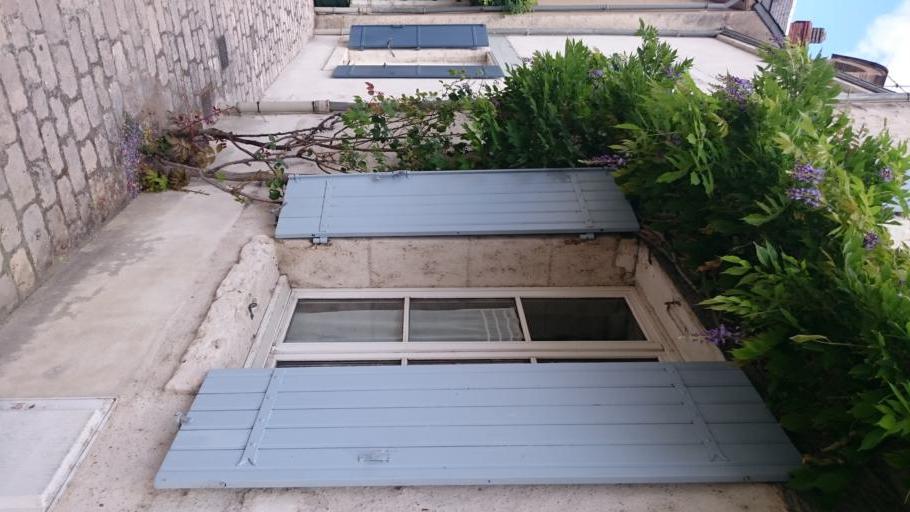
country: FR
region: Centre
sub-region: Departement du Loiret
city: Beaugency
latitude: 47.7789
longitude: 1.6318
